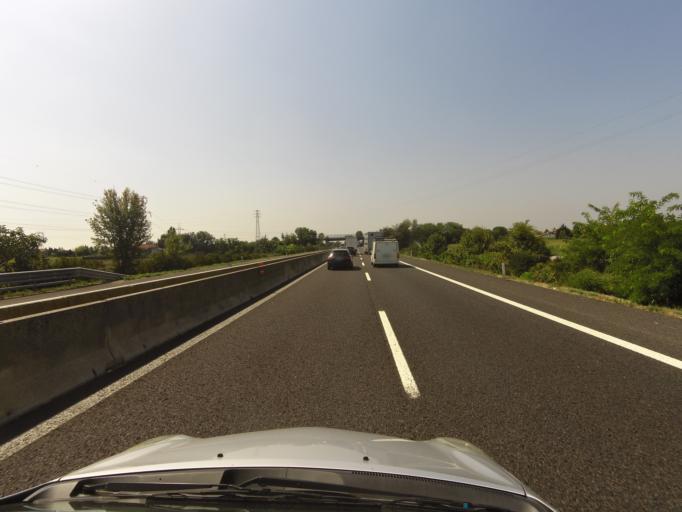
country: IT
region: Veneto
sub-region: Provincia di Padova
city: Ponte San Nicolo
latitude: 45.3638
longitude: 11.9464
